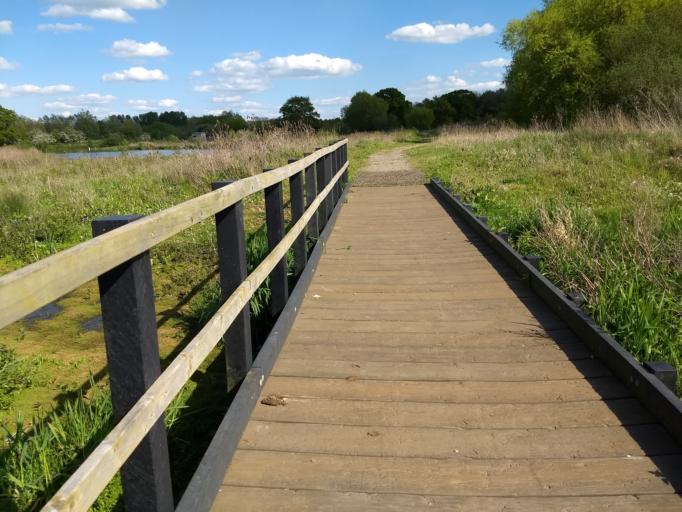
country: GB
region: England
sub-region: Milton Keynes
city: Castlethorpe
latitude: 52.0721
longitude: -0.8204
